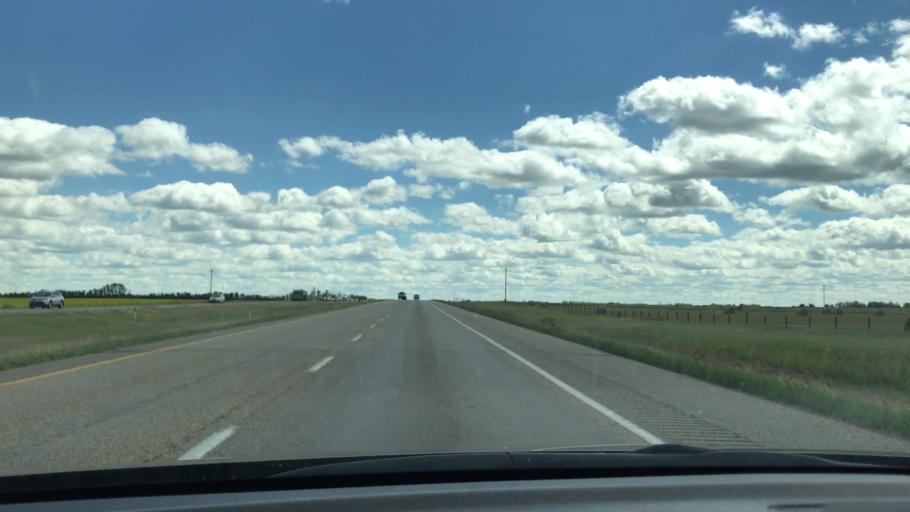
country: CA
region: Alberta
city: Leduc
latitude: 53.1658
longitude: -113.5982
